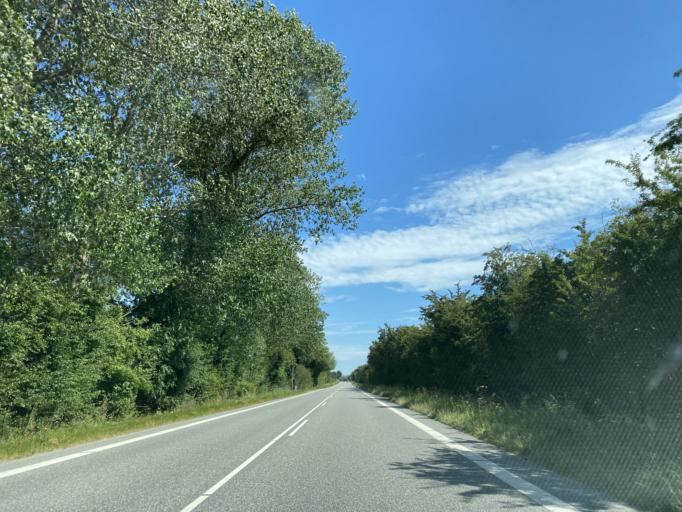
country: DK
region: South Denmark
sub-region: Faaborg-Midtfyn Kommune
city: Faaborg
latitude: 55.1076
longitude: 10.1408
